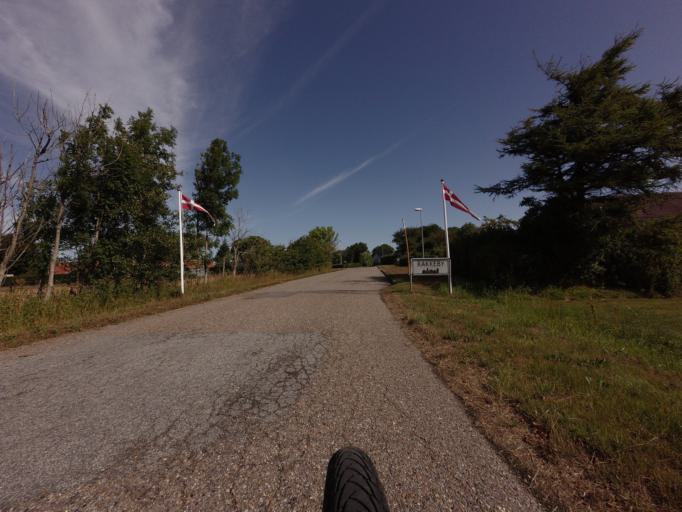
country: DK
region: North Denmark
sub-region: Hjorring Kommune
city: Vra
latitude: 57.4039
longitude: 9.9375
